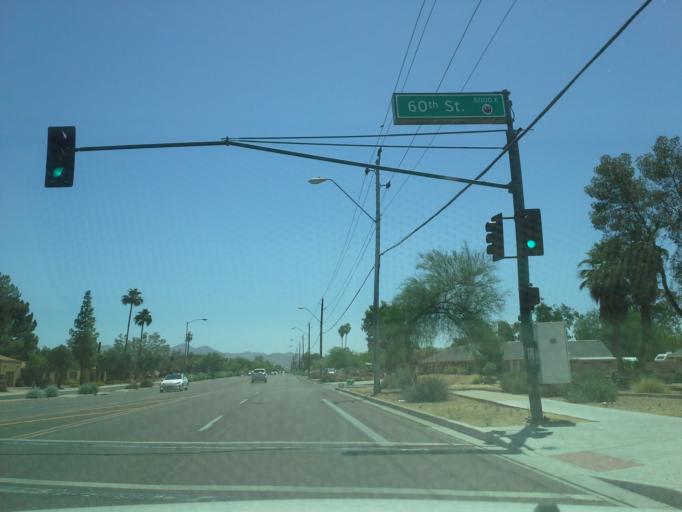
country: US
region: Arizona
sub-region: Maricopa County
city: Paradise Valley
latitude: 33.6113
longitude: -111.9519
